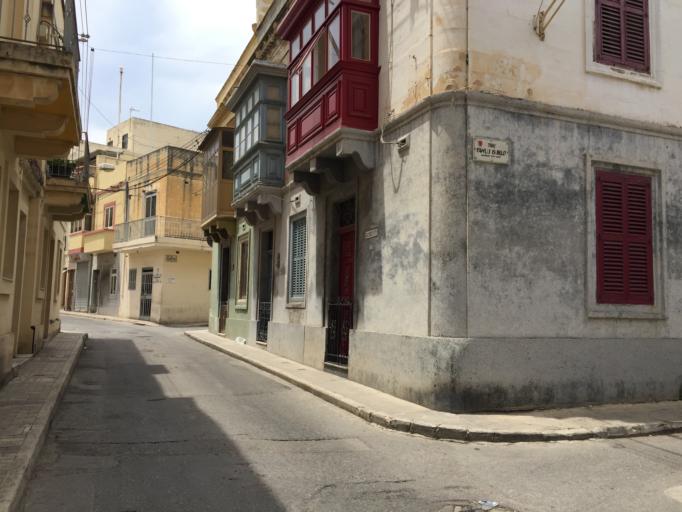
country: MT
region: Il-Hamrun
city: Hamrun
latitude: 35.8874
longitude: 14.4890
